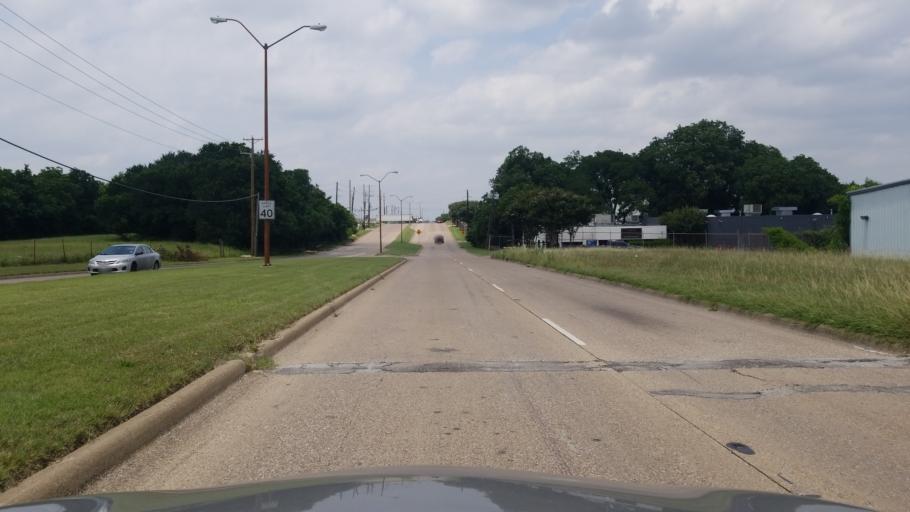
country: US
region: Texas
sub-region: Dallas County
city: Duncanville
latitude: 32.6883
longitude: -96.9085
